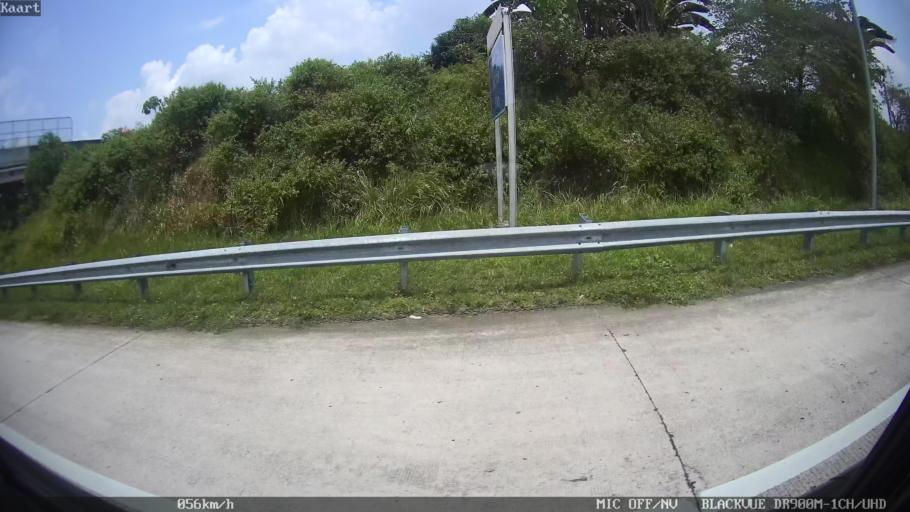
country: ID
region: Lampung
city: Natar
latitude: -5.2773
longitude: 105.2160
